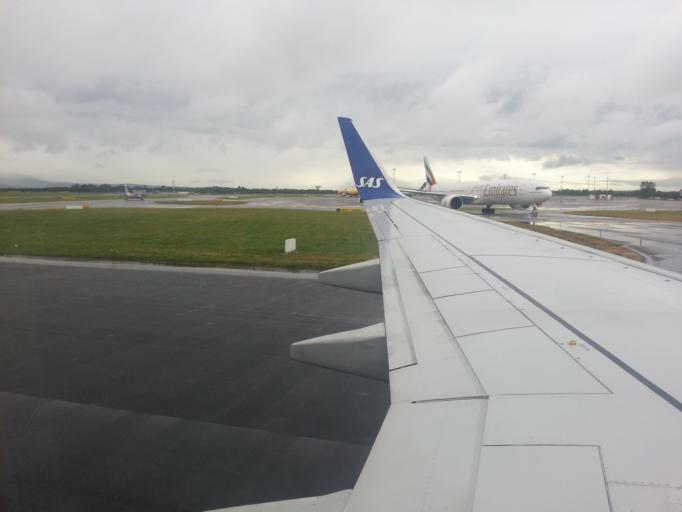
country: IE
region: Leinster
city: Ballymun
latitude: 53.4276
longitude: -6.2552
